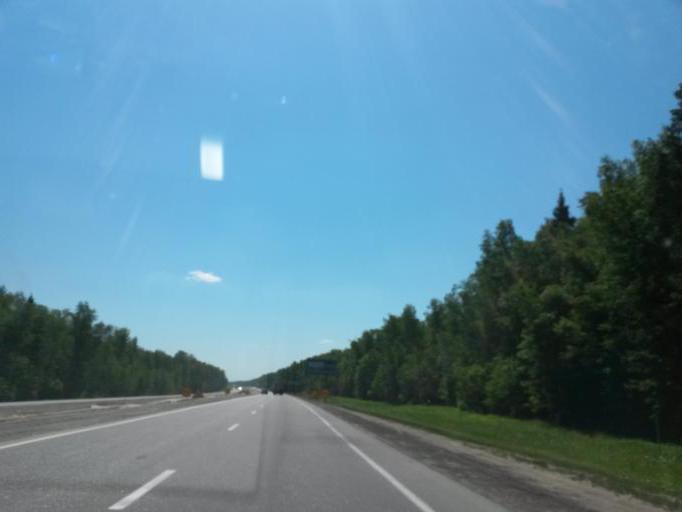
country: RU
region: Moskovskaya
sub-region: Chekhovskiy Rayon
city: Chekhov
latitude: 55.1778
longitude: 37.5363
